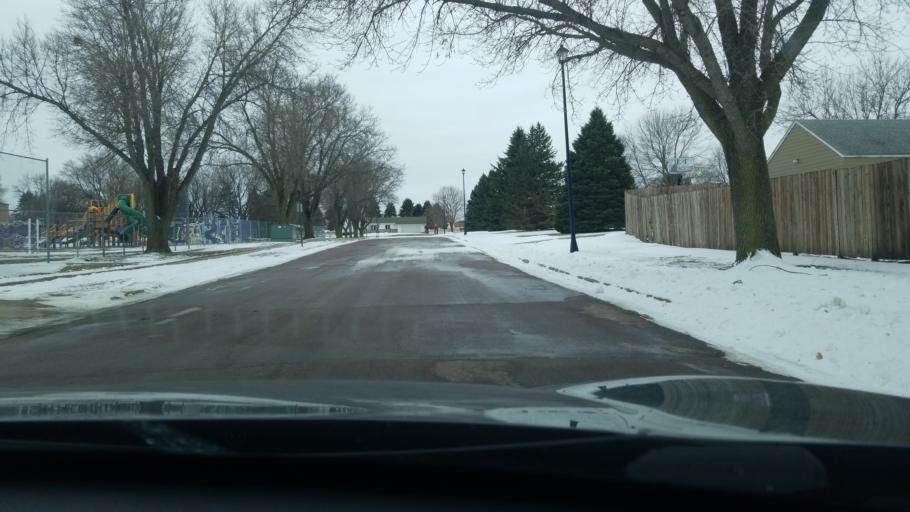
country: US
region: Iowa
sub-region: Lyon County
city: Rock Rapids
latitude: 43.4203
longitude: -96.1707
